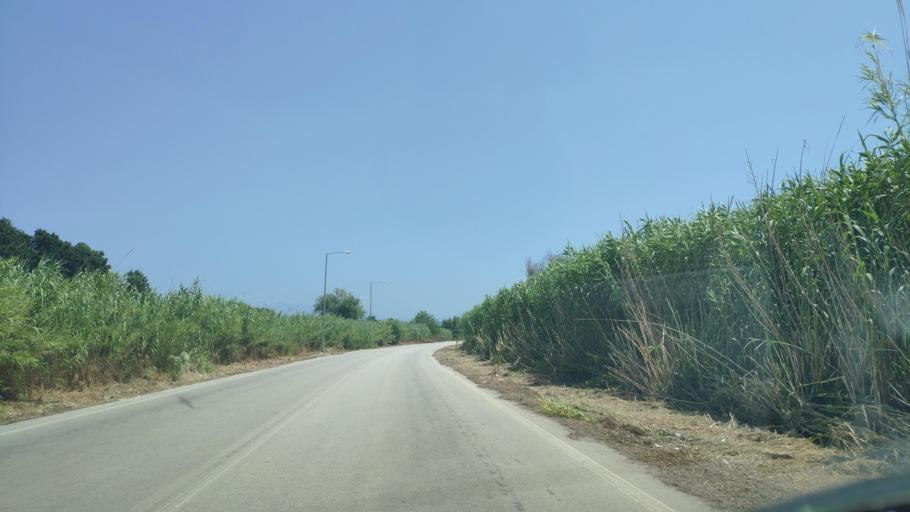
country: GR
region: Epirus
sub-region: Nomos Artas
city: Aneza
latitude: 39.0909
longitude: 20.9006
